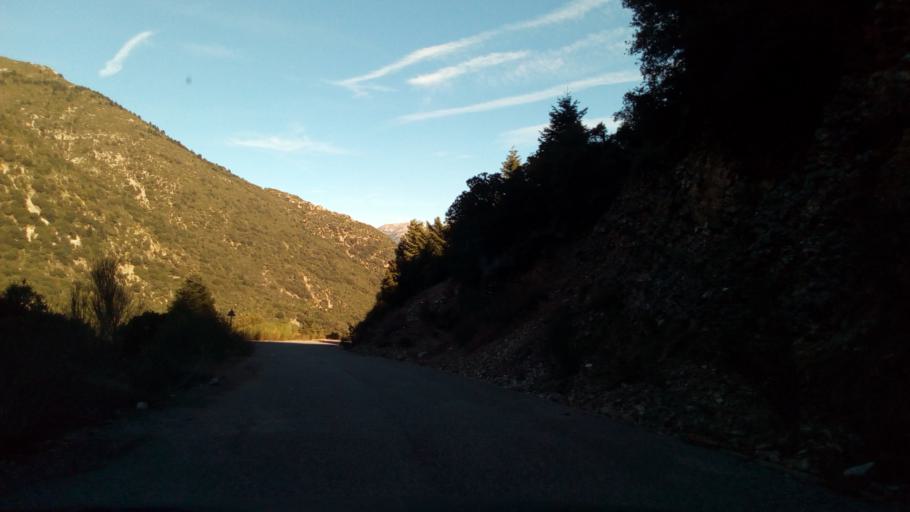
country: GR
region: West Greece
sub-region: Nomos Aitolias kai Akarnanias
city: Nafpaktos
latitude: 38.5438
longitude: 21.8530
